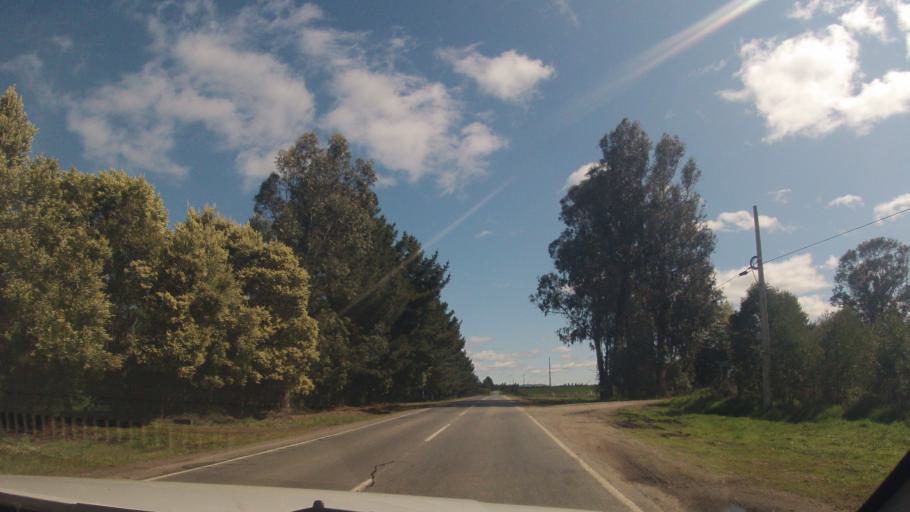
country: CL
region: Araucania
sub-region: Provincia de Malleco
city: Traiguen
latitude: -38.2621
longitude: -72.6321
